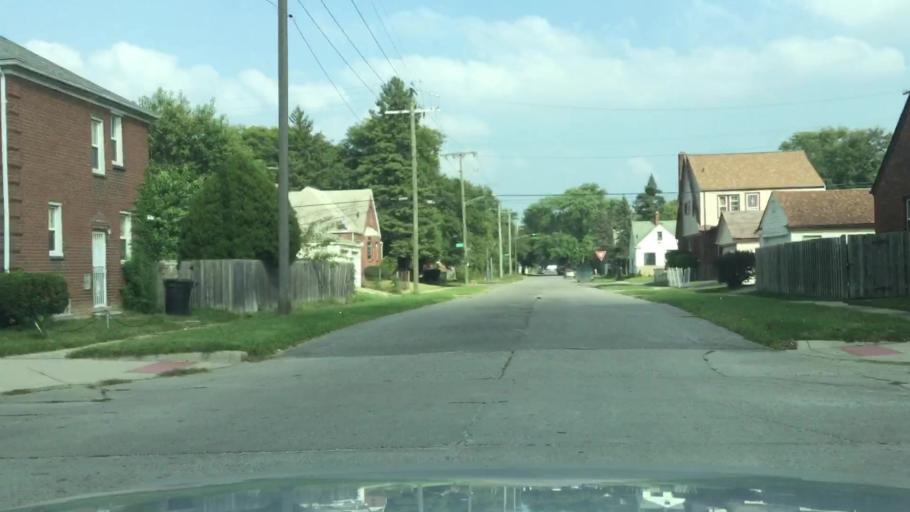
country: US
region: Michigan
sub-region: Wayne County
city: Dearborn
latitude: 42.3535
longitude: -83.1935
